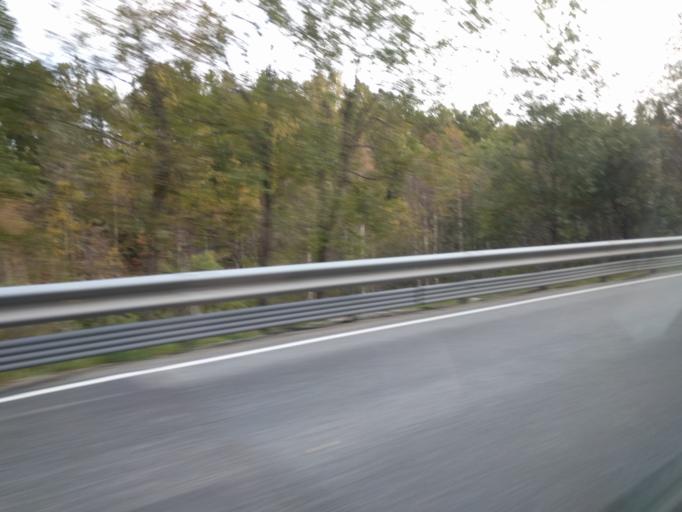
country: NO
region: Vest-Agder
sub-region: Kristiansand
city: Strai
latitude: 58.2539
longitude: 7.8569
